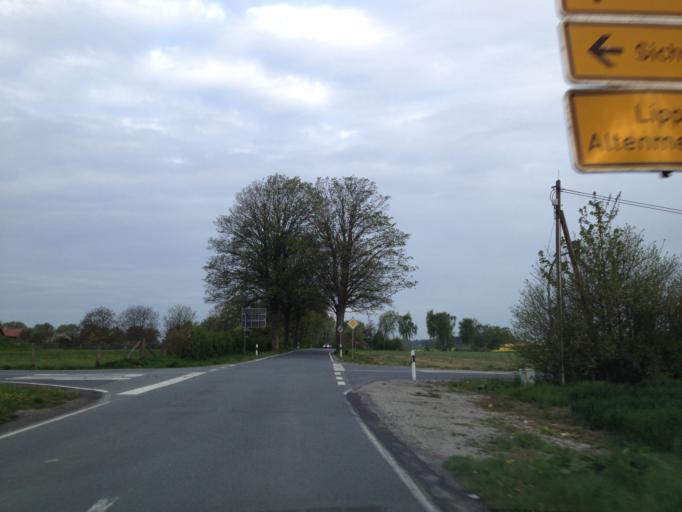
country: DE
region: North Rhine-Westphalia
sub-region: Regierungsbezirk Arnsberg
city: Anrochte
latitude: 51.5087
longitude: 8.2669
